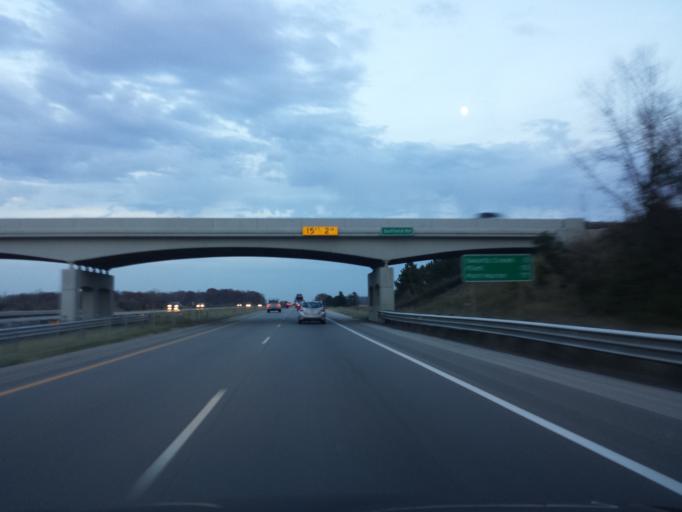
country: US
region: Michigan
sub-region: Genesee County
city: Swartz Creek
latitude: 42.9644
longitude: -83.9099
